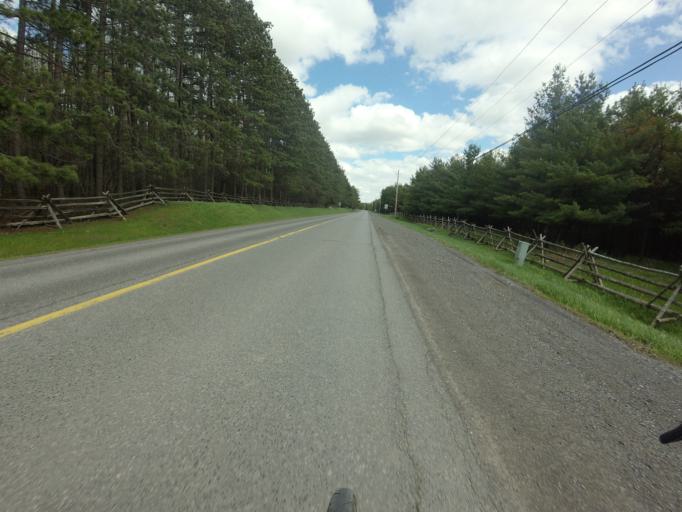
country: CA
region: Ontario
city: Bells Corners
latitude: 45.3438
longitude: -76.0186
